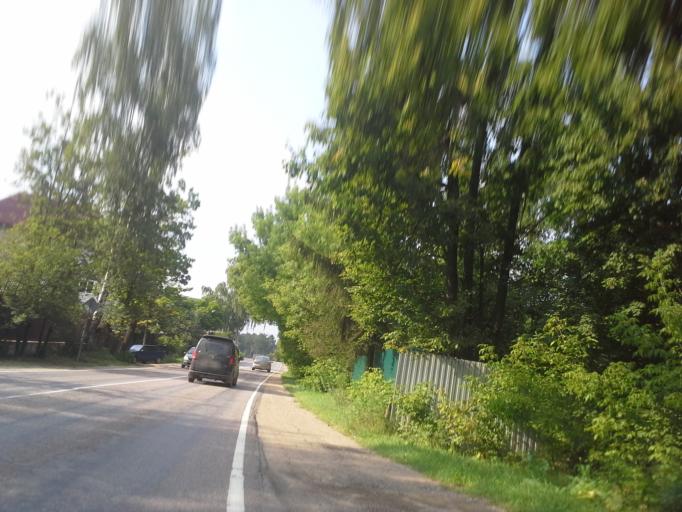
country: RU
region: Moskovskaya
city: Istra
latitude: 55.8883
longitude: 36.7972
